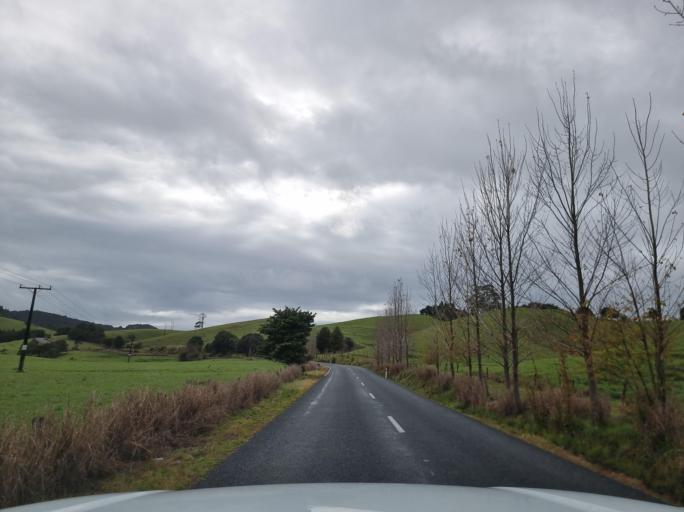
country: NZ
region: Northland
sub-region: Whangarei
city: Ruakaka
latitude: -35.9317
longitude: 174.4157
